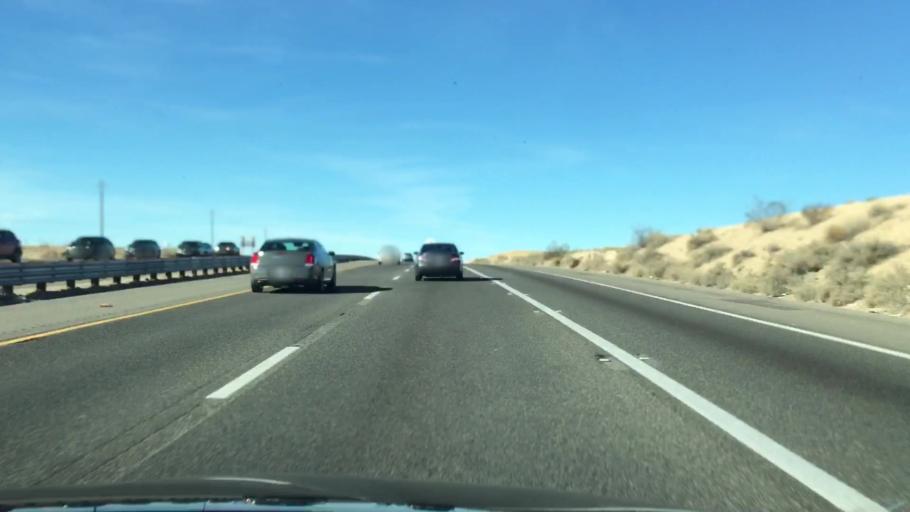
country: US
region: California
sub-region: San Bernardino County
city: Barstow
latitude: 34.9039
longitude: -116.9361
